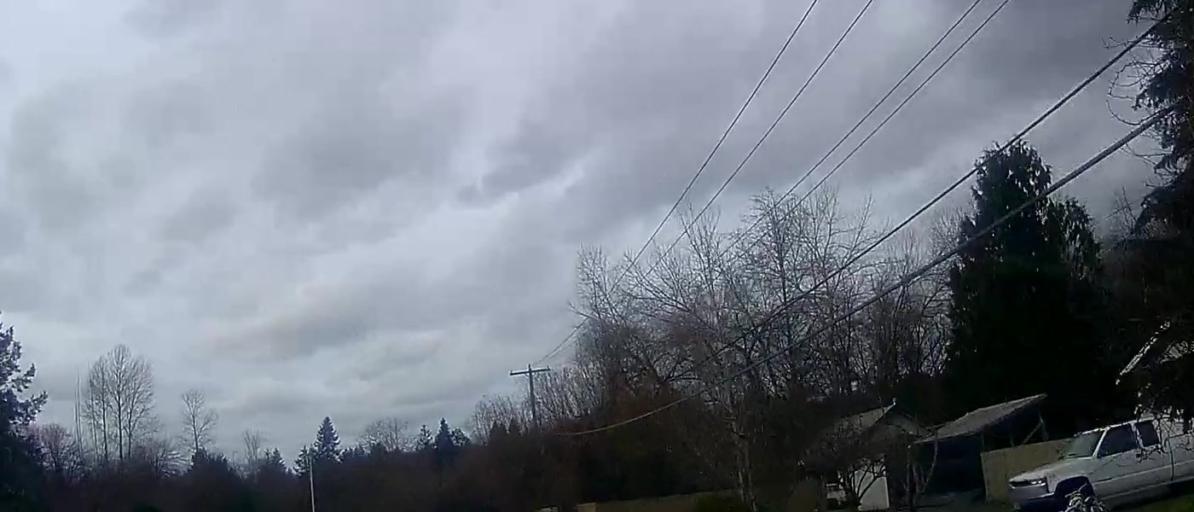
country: US
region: Washington
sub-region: Skagit County
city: Sedro-Woolley
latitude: 48.5831
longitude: -122.2806
